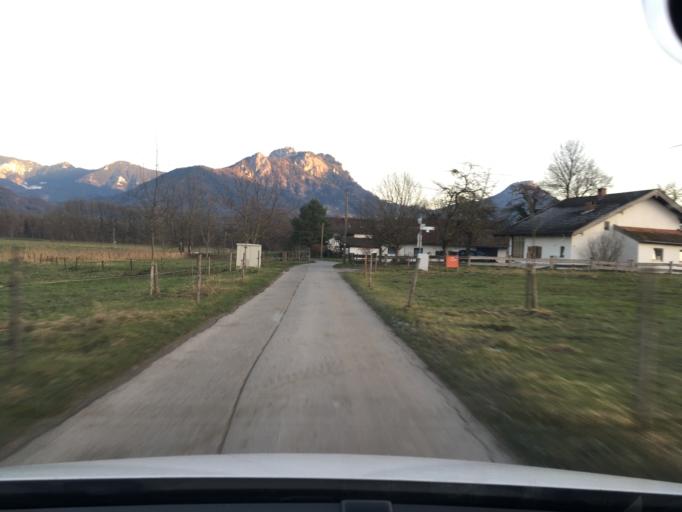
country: DE
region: Bavaria
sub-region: Upper Bavaria
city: Flintsbach
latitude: 47.7472
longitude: 12.1225
